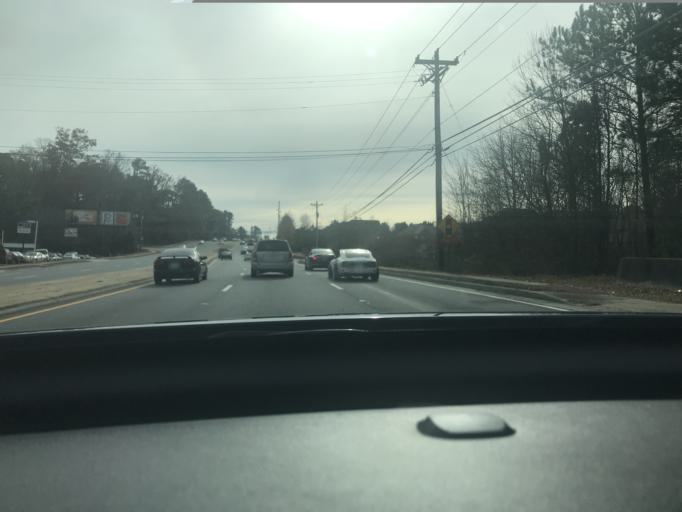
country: US
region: Georgia
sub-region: Gwinnett County
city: Lilburn
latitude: 33.9223
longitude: -84.1141
